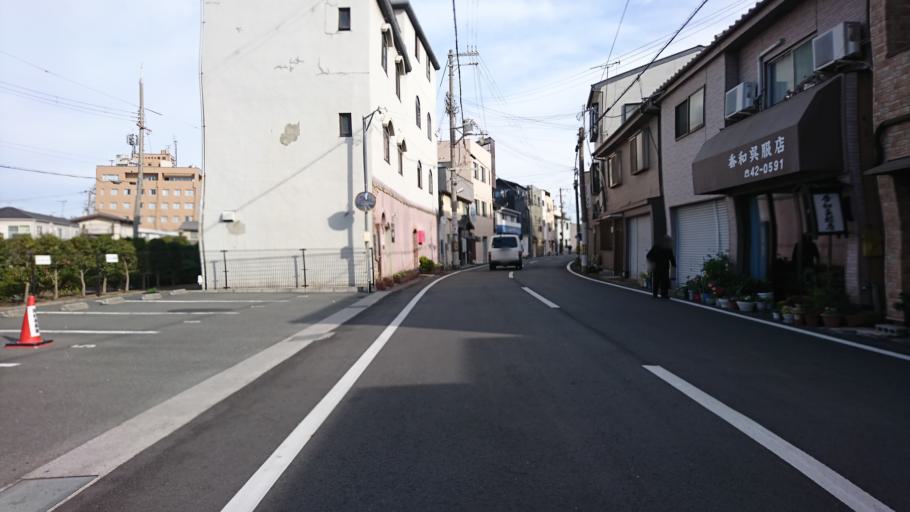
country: JP
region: Hyogo
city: Kakogawacho-honmachi
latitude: 34.7499
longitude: 134.8018
